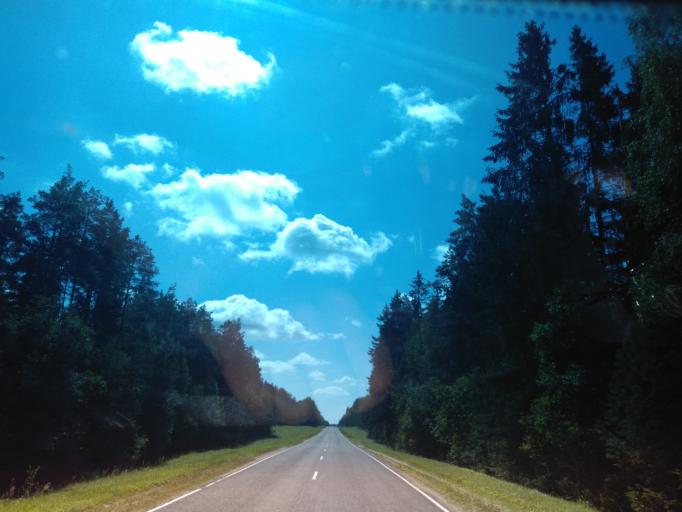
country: BY
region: Minsk
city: Uzda
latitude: 53.3283
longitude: 27.2312
